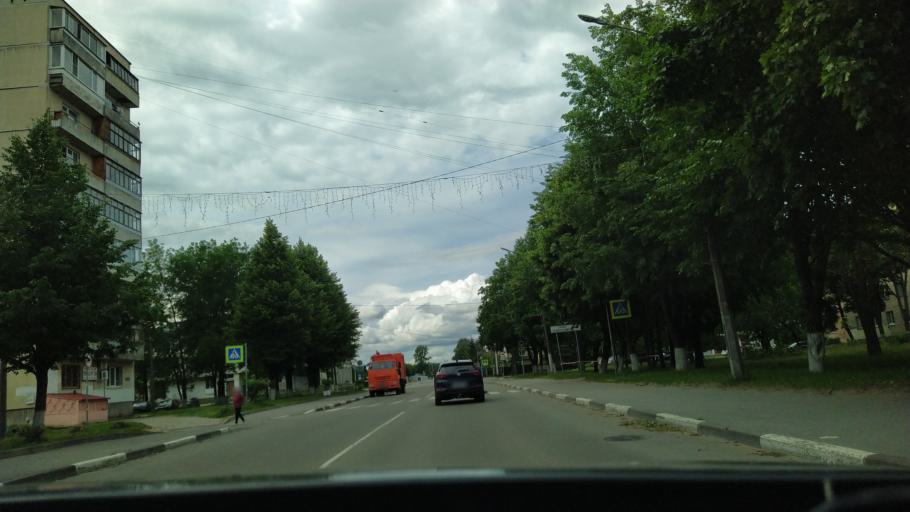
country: RU
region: Leningrad
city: Kirovsk
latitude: 59.8811
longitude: 30.9899
